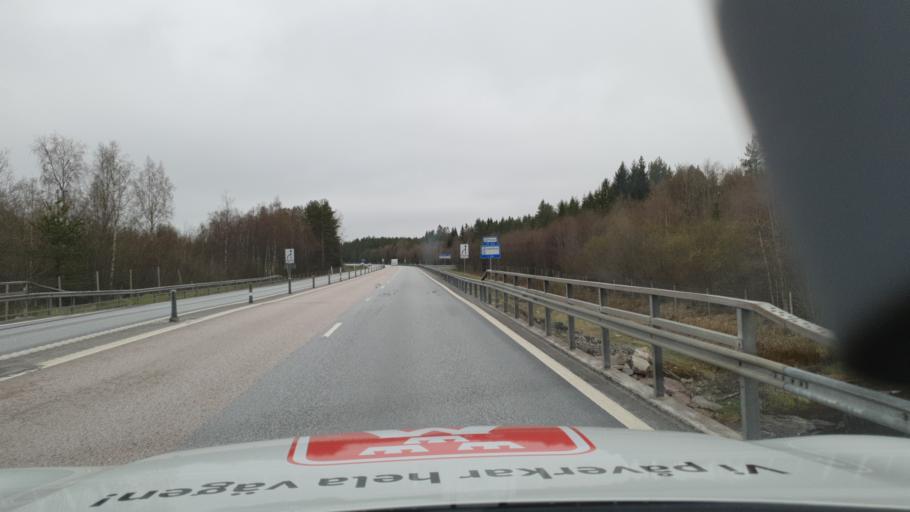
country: SE
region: Vaesterbotten
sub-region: Nordmalings Kommun
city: Nordmaling
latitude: 63.5687
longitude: 19.4350
